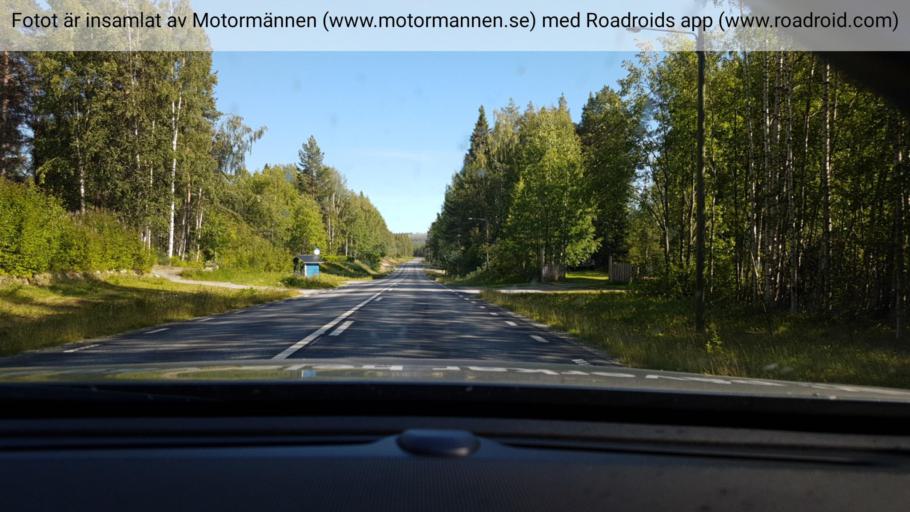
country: SE
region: Vaesterbotten
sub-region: Lycksele Kommun
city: Lycksele
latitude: 64.5402
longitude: 18.7533
